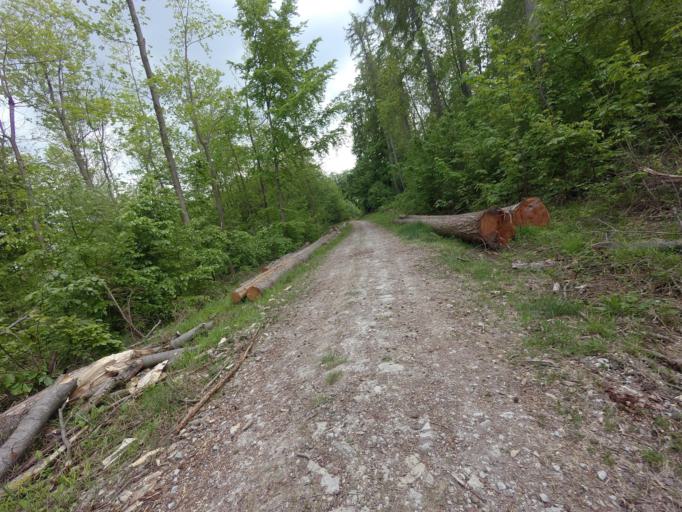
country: DE
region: Lower Saxony
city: Diekholzen
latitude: 52.1191
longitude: 9.9146
